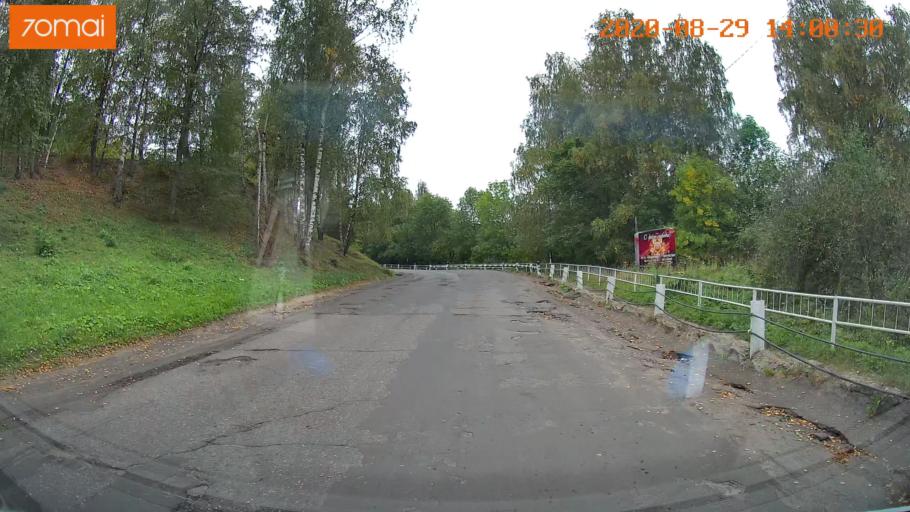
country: RU
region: Ivanovo
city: Yur'yevets
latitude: 57.3146
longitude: 43.1084
